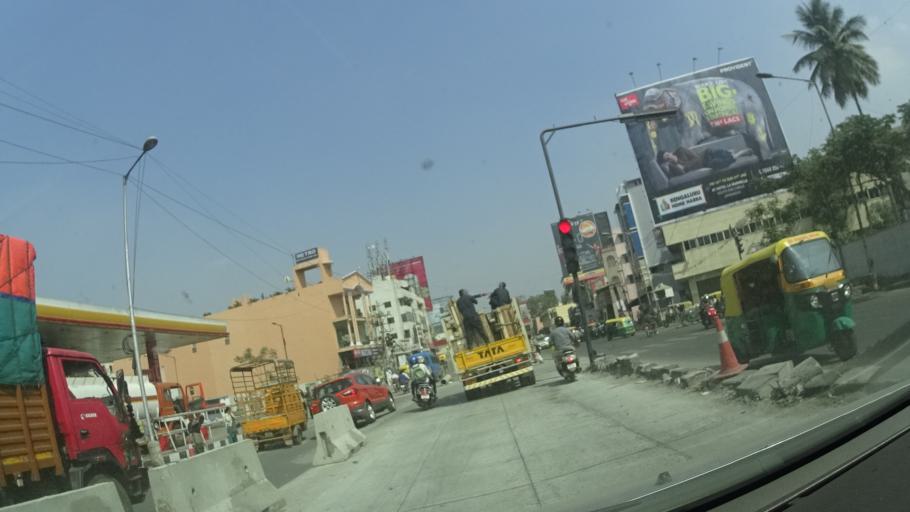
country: IN
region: Karnataka
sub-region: Bangalore Urban
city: Bangalore
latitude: 12.9573
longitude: 77.5517
